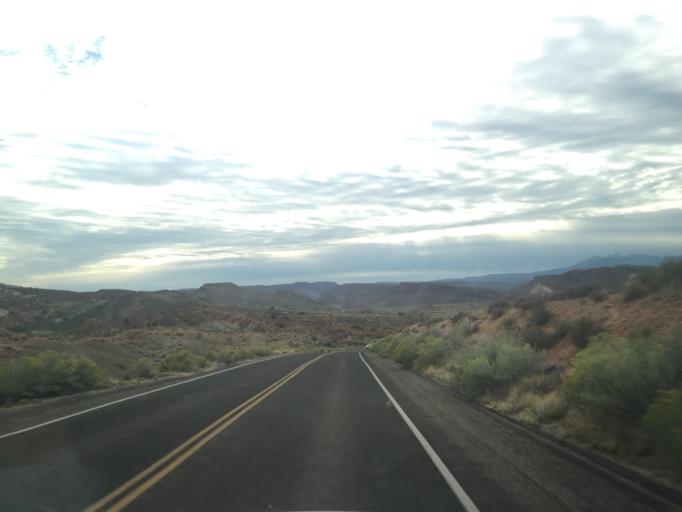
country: US
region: Utah
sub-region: Grand County
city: Moab
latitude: 38.7368
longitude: -109.5648
